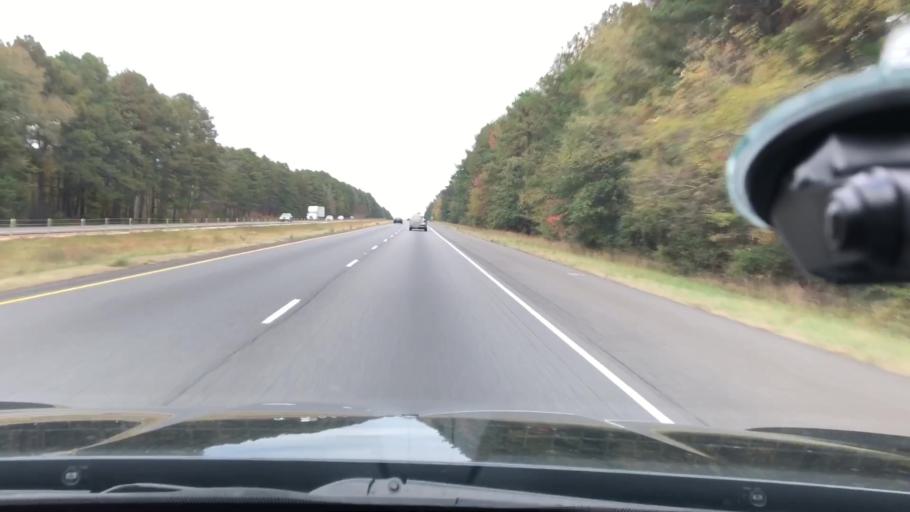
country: US
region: Arkansas
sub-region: Clark County
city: Arkadelphia
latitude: 34.2677
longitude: -92.9741
